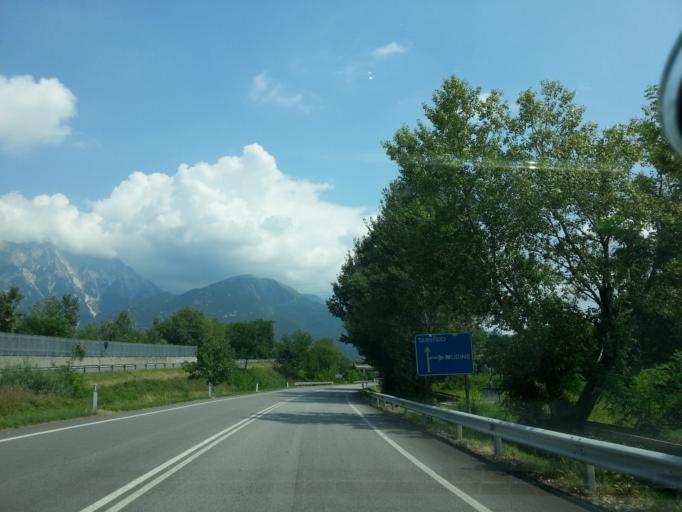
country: IT
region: Friuli Venezia Giulia
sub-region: Provincia di Udine
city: Osoppo
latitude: 46.2584
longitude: 13.1057
